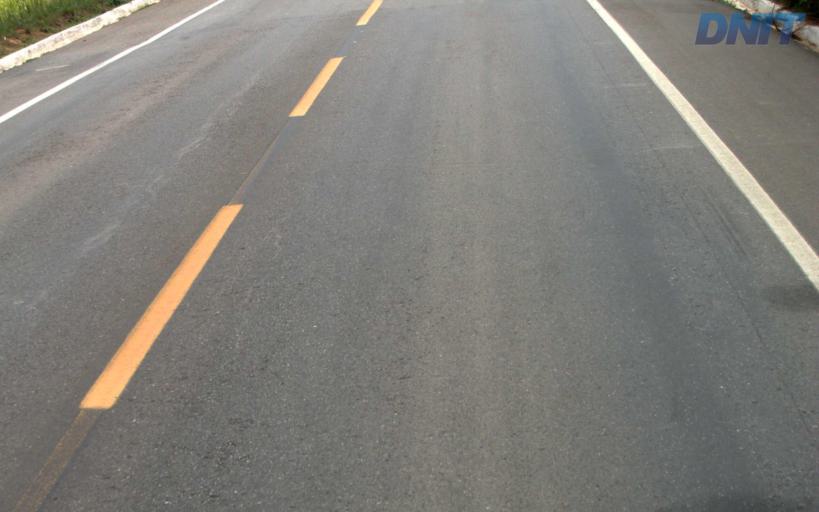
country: BR
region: Minas Gerais
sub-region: Governador Valadares
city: Governador Valadares
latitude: -18.9319
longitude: -42.0472
